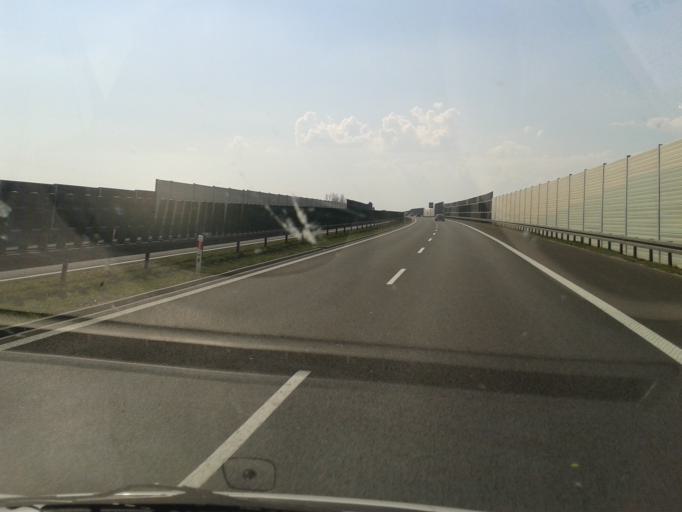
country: PL
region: Lesser Poland Voivodeship
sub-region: Powiat tarnowski
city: Niedomice
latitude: 50.0566
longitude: 20.9212
